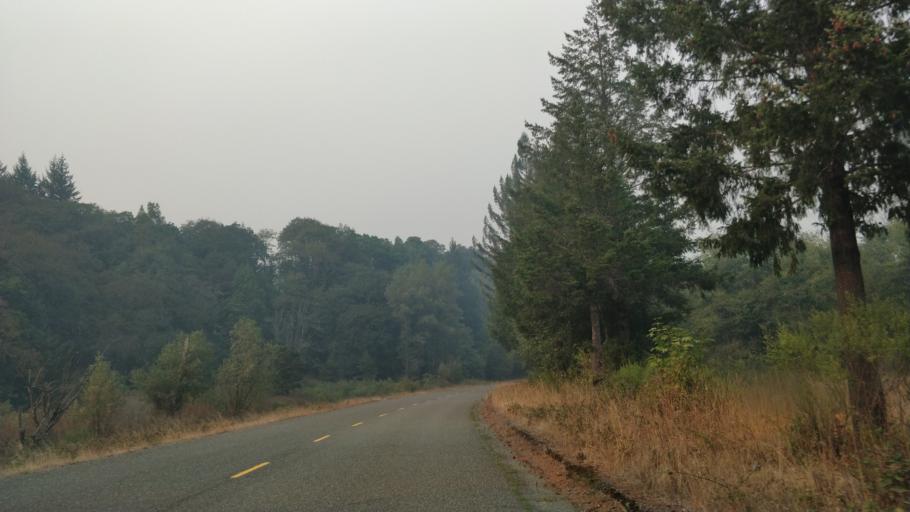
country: US
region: California
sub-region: Humboldt County
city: Rio Dell
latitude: 40.3373
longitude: -124.0273
